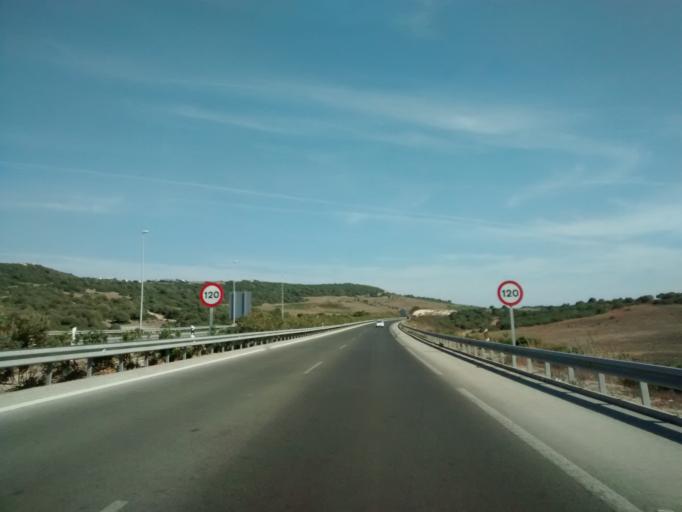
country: ES
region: Andalusia
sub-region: Provincia de Cadiz
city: Conil de la Frontera
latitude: 36.3130
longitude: -6.0569
